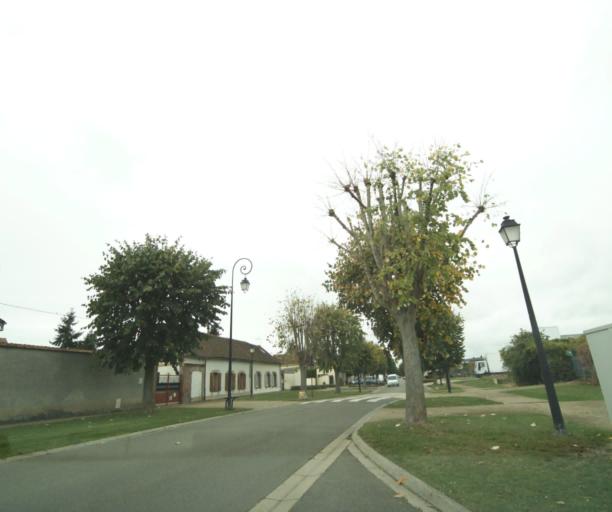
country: FR
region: Centre
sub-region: Departement d'Eure-et-Loir
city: Dreux
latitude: 48.7411
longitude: 1.3429
